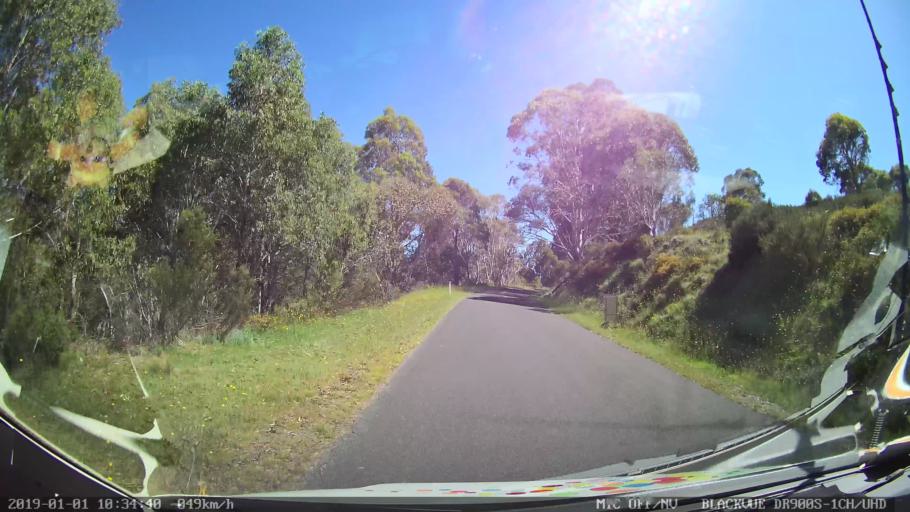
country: AU
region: New South Wales
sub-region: Snowy River
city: Jindabyne
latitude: -36.0489
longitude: 148.2843
